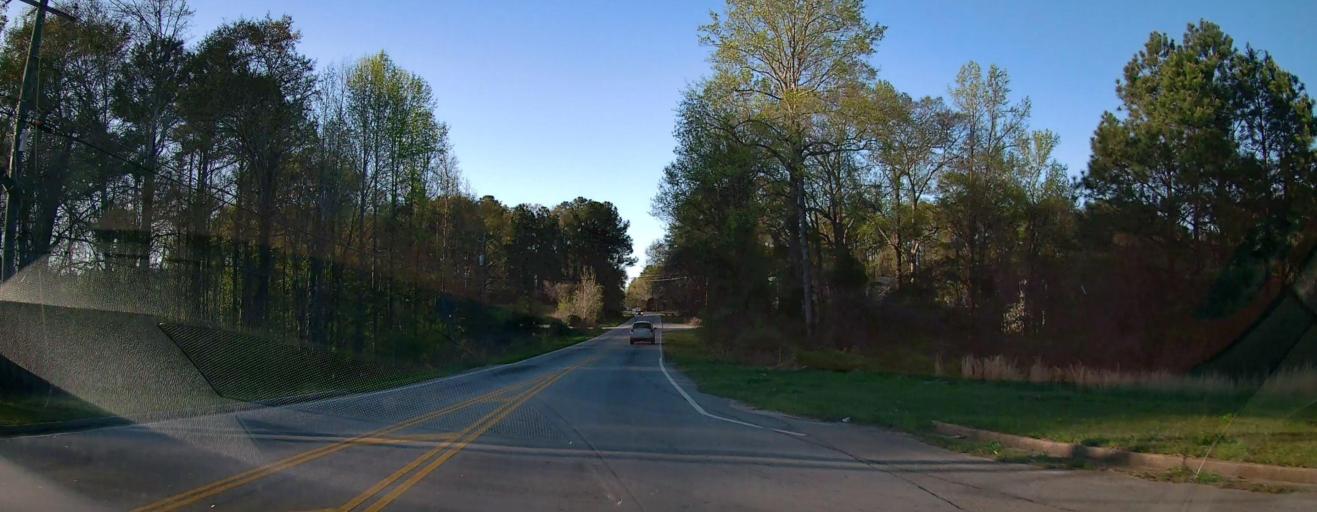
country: US
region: Georgia
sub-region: Newton County
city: Porterdale
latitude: 33.5667
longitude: -83.9025
